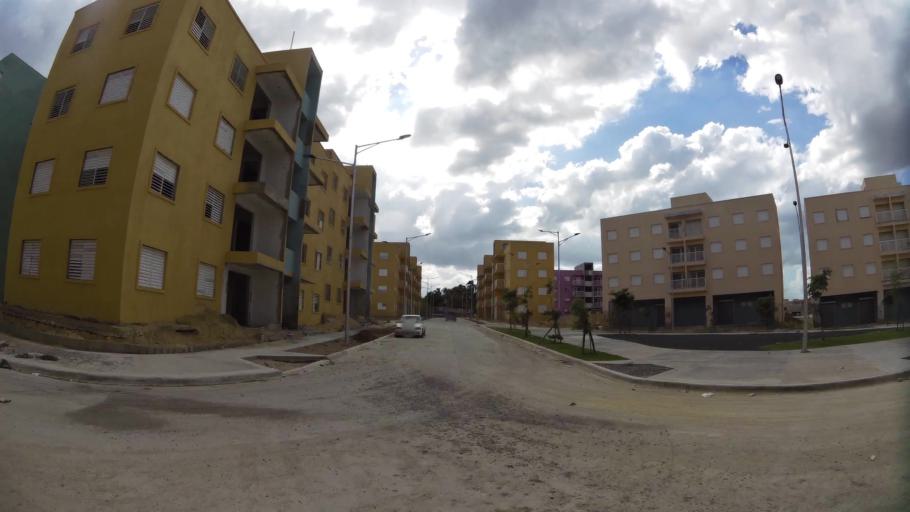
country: DO
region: Nacional
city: Ensanche Luperon
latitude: 18.5282
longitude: -69.8819
